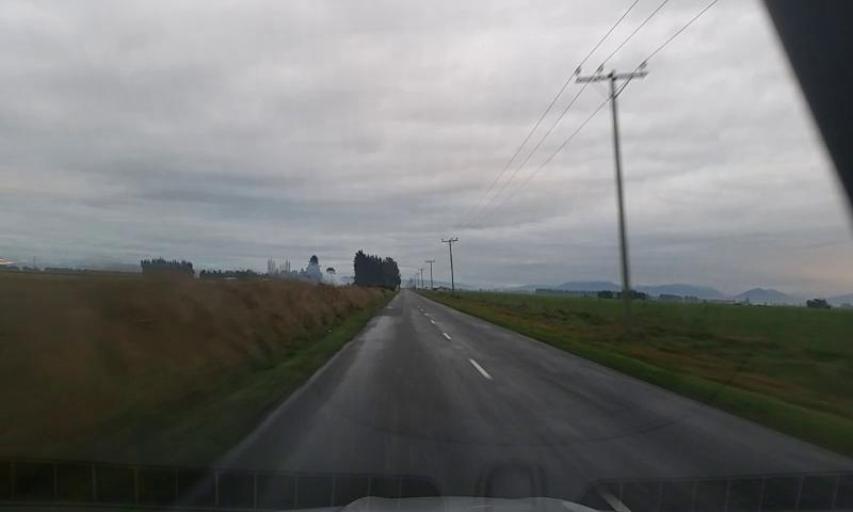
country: NZ
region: Canterbury
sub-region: Ashburton District
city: Ashburton
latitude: -43.7506
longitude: 171.8332
